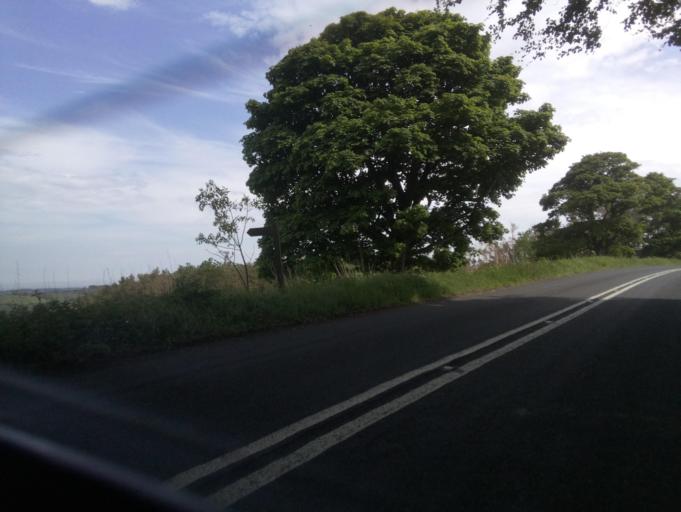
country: GB
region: England
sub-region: Northumberland
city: Alnwick
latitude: 55.4535
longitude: -1.7114
